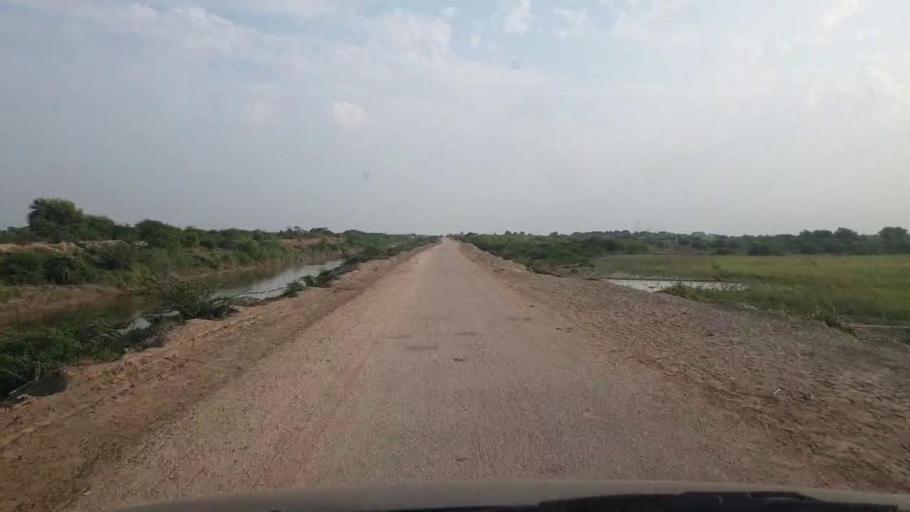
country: PK
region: Sindh
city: Badin
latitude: 24.5375
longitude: 68.6758
